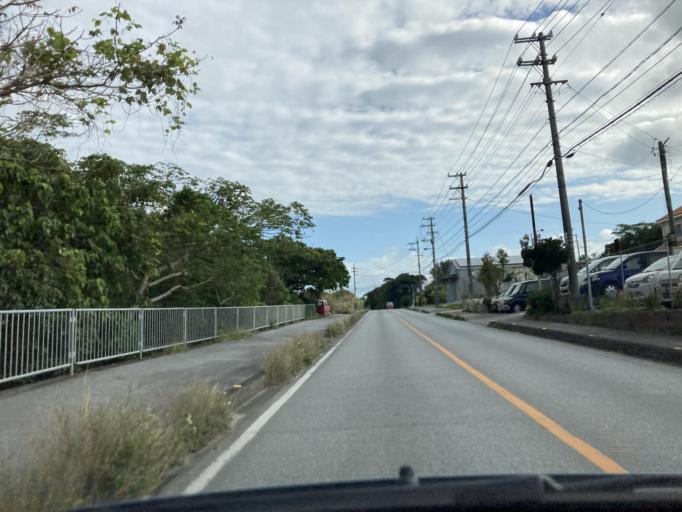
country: JP
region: Okinawa
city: Nago
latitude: 26.6621
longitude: 127.9802
